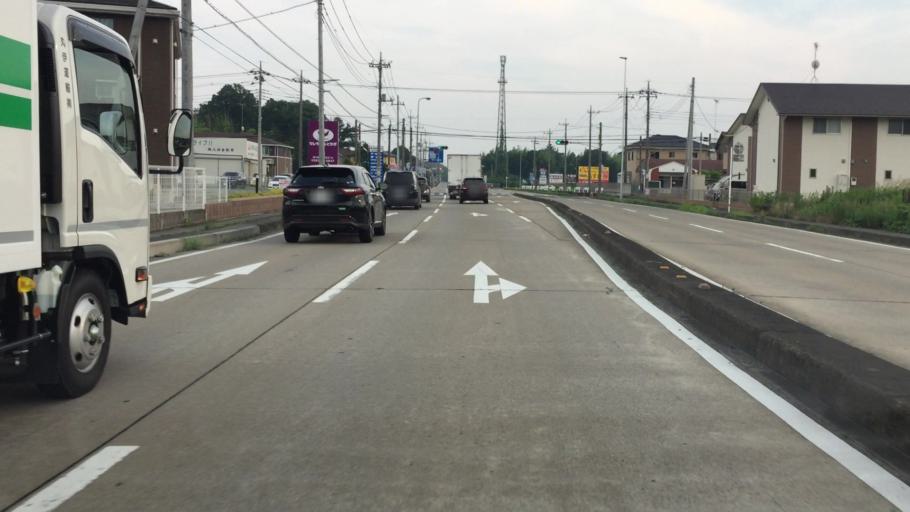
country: JP
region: Tochigi
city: Tochigi
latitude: 36.3409
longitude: 139.6961
